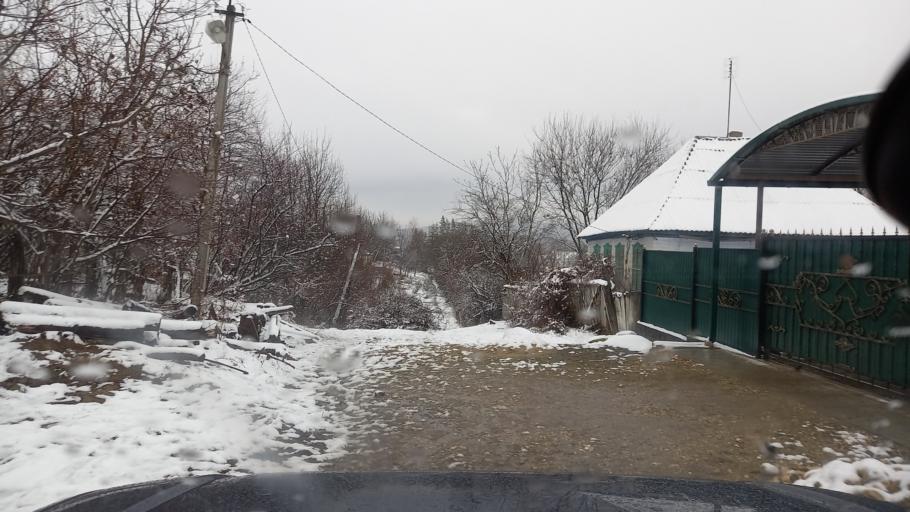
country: RU
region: Adygeya
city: Abadzekhskaya
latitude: 44.3506
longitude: 40.4083
